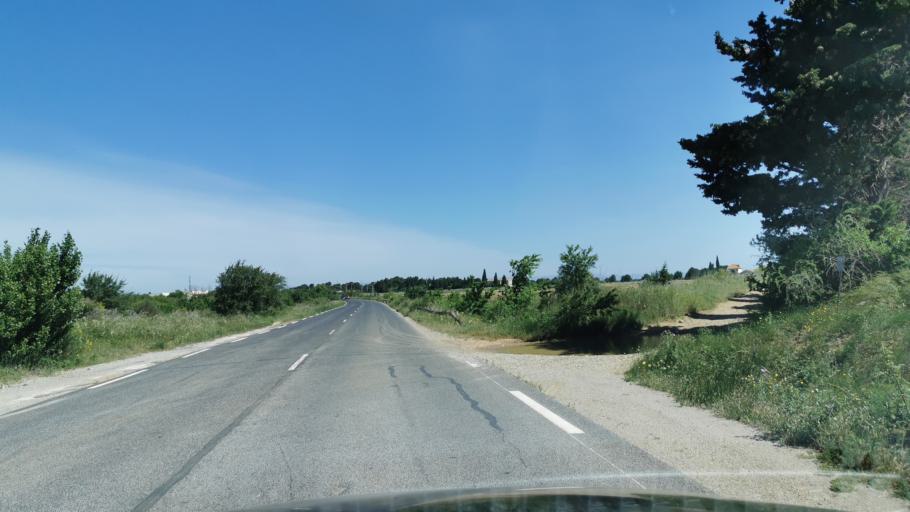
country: FR
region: Languedoc-Roussillon
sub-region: Departement de l'Aude
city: Narbonne
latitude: 43.1530
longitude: 2.9976
